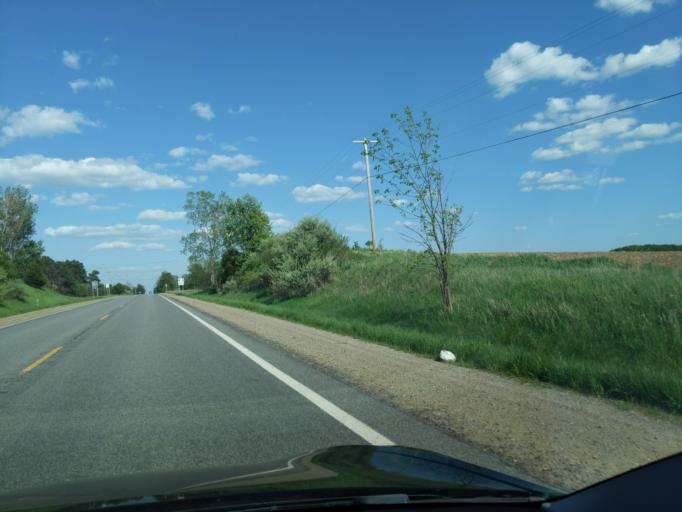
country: US
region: Michigan
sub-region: Ionia County
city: Portland
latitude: 42.7556
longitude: -84.9384
